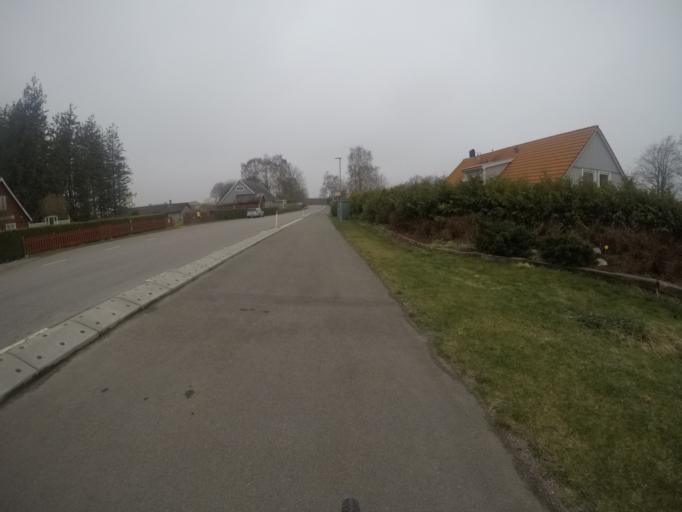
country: SE
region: Skane
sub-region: Angelholms Kommun
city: Strovelstorp
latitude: 56.2215
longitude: 12.7567
